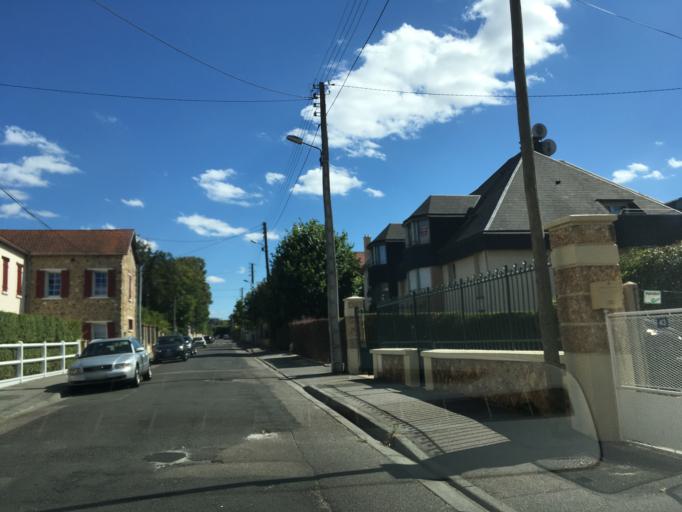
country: FR
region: Haute-Normandie
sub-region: Departement de l'Eure
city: Vernon
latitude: 49.0877
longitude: 1.4761
